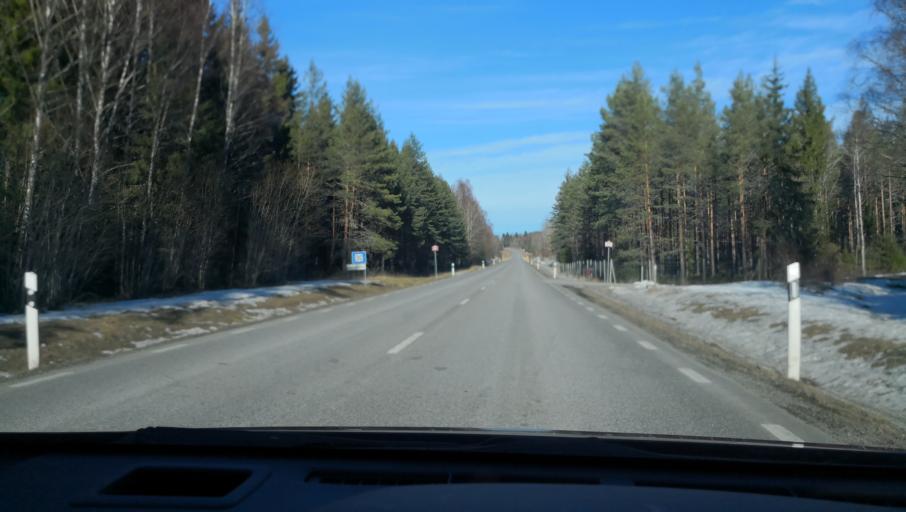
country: SE
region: Uppsala
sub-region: Uppsala Kommun
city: Vattholma
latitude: 60.0556
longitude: 17.7529
